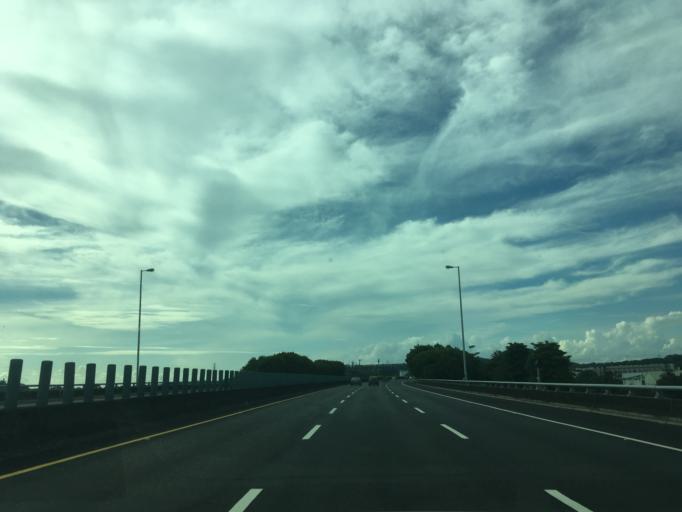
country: TW
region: Taiwan
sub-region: Chiayi
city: Jiayi Shi
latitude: 23.5089
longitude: 120.4878
